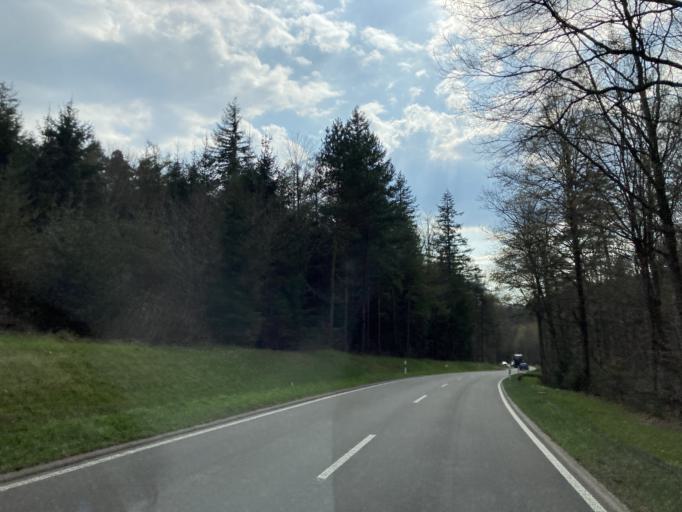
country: DE
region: Baden-Wuerttemberg
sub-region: Karlsruhe Region
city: Ettlingen
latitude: 48.8861
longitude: 8.4698
